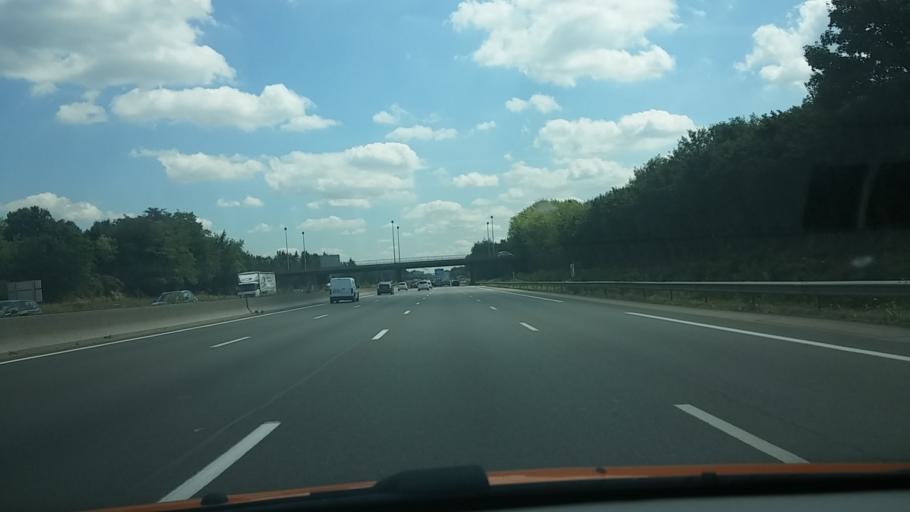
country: FR
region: Ile-de-France
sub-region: Departement du Val-de-Marne
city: Villiers-sur-Marne
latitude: 48.8359
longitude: 2.5598
